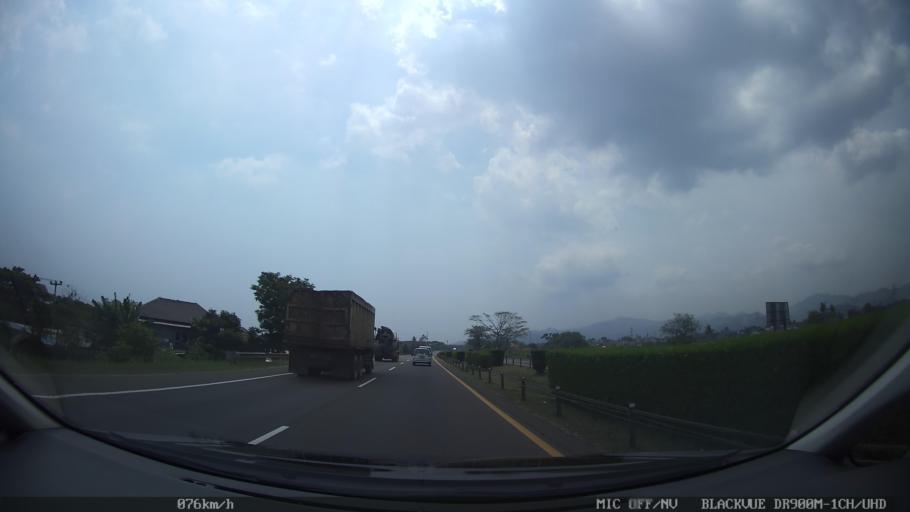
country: ID
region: Banten
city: Bojonegara
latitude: -6.0093
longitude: 106.0721
